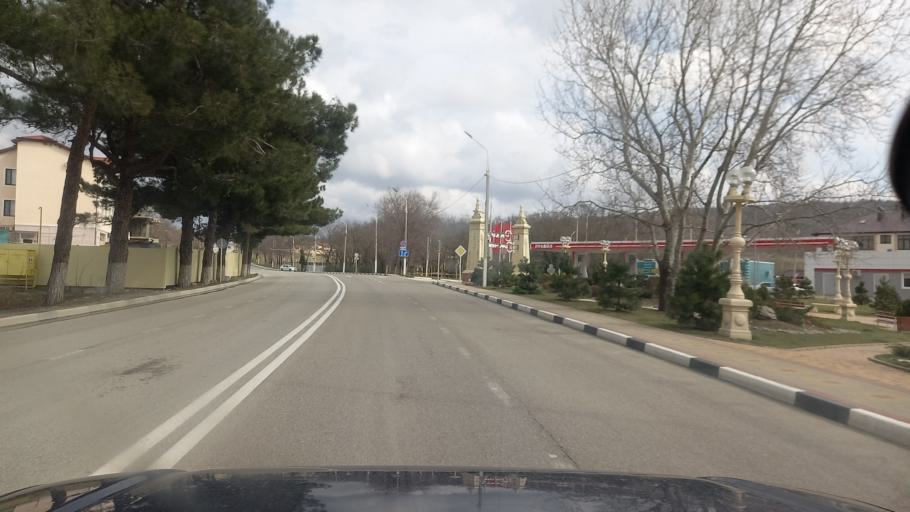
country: RU
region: Krasnodarskiy
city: Gelendzhik
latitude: 44.5548
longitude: 38.1098
